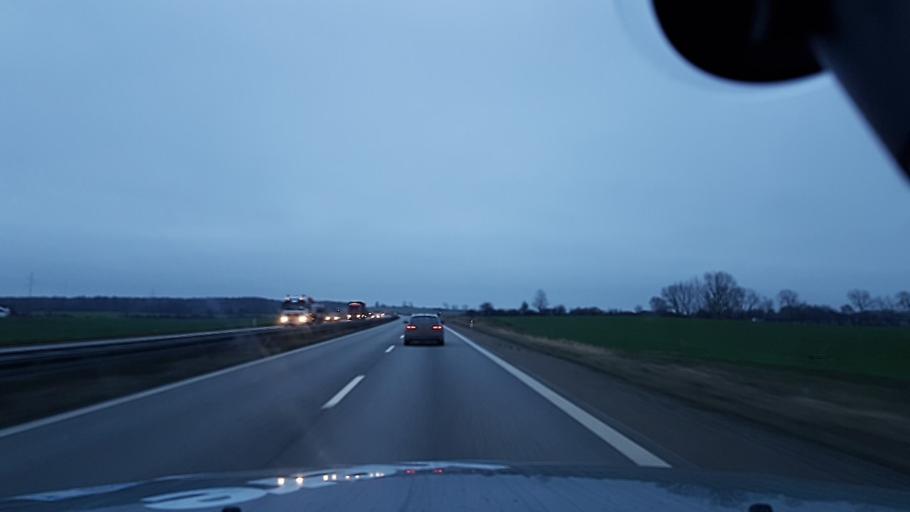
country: DK
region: Zealand
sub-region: Vordingborg Kommune
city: Orslev
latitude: 55.1079
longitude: 11.9358
